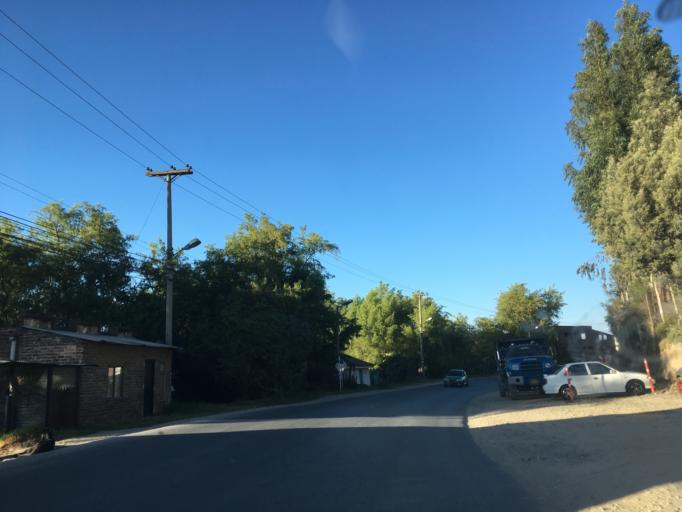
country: CO
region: Boyaca
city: Sogamoso
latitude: 5.6981
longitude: -72.9404
